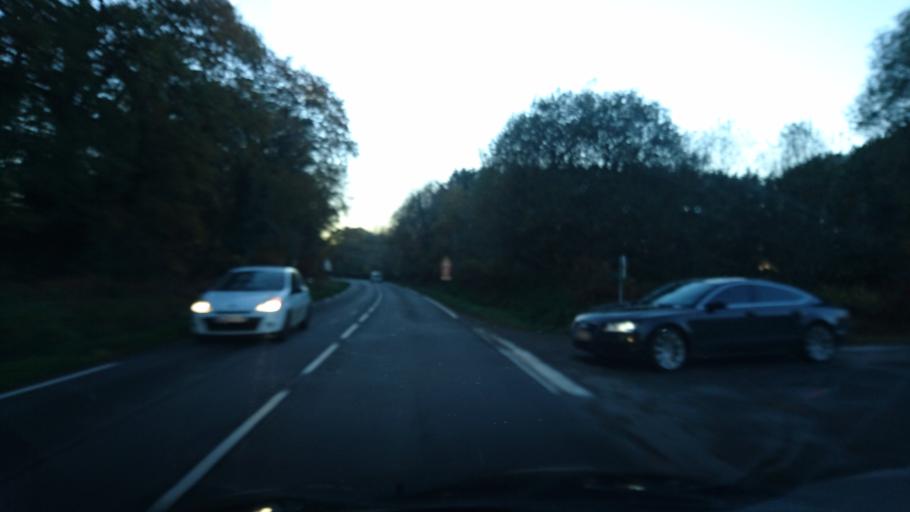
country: FR
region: Brittany
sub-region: Departement du Finistere
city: Quimperle
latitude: 47.8477
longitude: -3.5751
